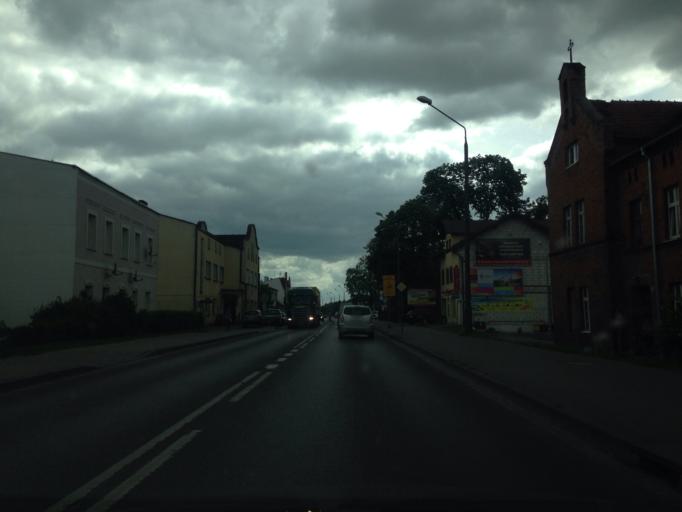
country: PL
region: Kujawsko-Pomorskie
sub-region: Powiat swiecki
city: Swiecie
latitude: 53.4033
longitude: 18.4097
